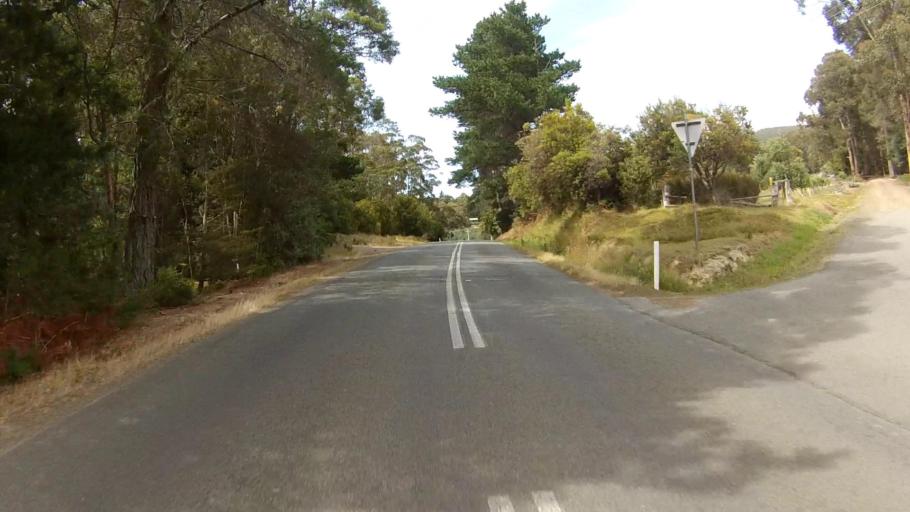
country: AU
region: Tasmania
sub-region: Kingborough
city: Kettering
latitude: -43.1892
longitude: 147.2452
